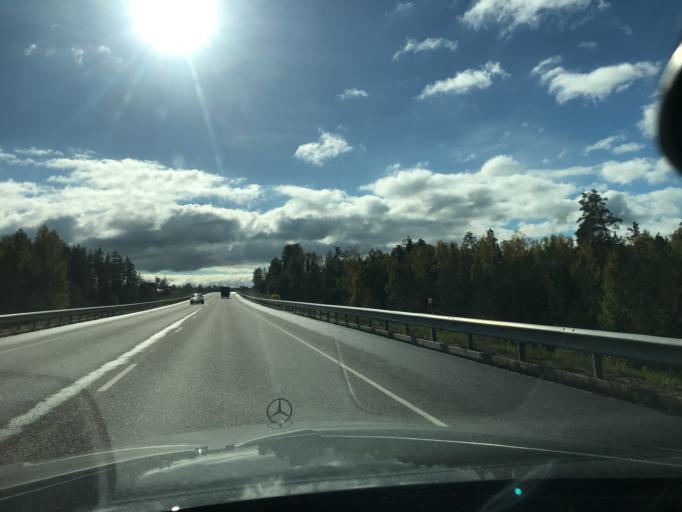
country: EE
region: Vorumaa
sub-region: Voru linn
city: Voru
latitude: 57.8208
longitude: 27.0641
